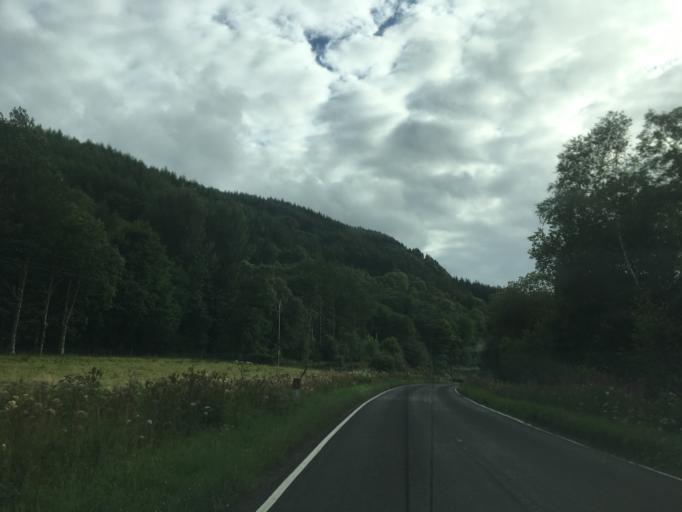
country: GB
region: Scotland
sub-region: Argyll and Bute
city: Oban
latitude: 56.3588
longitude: -5.4558
